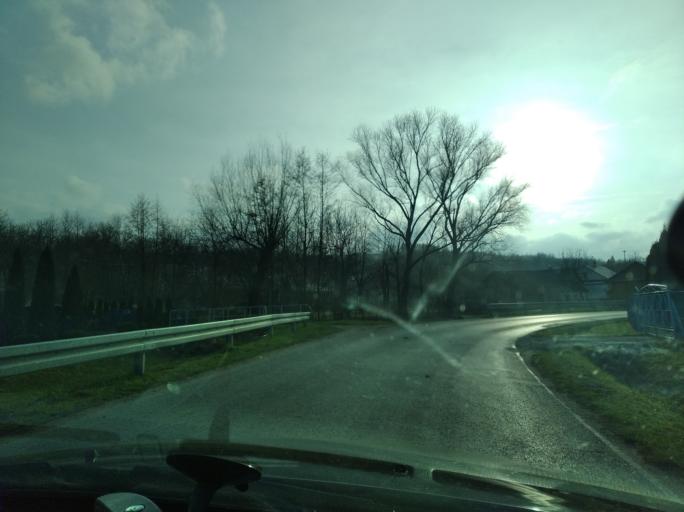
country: PL
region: Subcarpathian Voivodeship
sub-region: Powiat przeworski
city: Lopuszka Wielka
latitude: 49.9395
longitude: 22.4014
